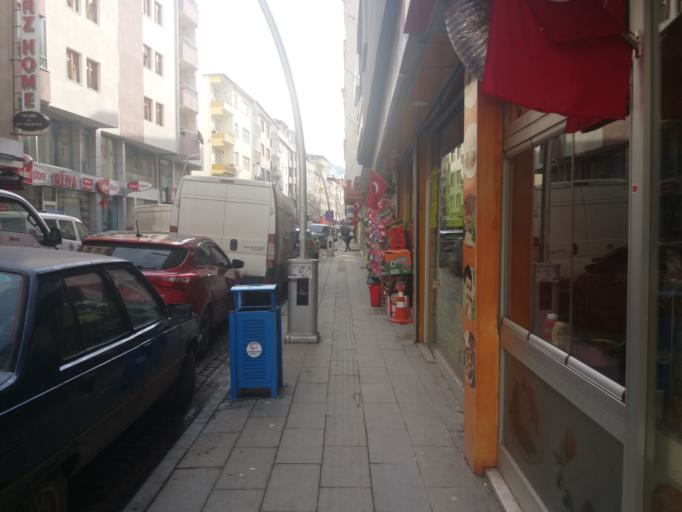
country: TR
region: Gumushane
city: Gumushkhane
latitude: 40.4610
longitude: 39.4738
